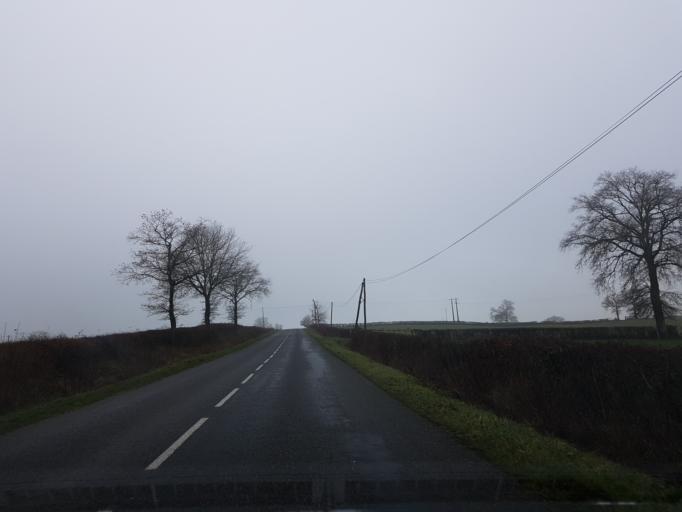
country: FR
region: Bourgogne
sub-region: Departement de Saone-et-Loire
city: Saint-Berain-sous-Sanvignes
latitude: 46.7323
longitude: 4.3338
